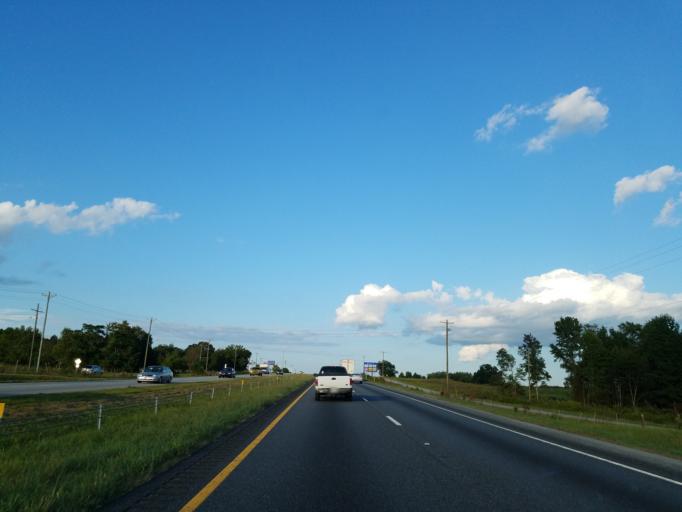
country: US
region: South Carolina
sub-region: Cherokee County
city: Gaffney
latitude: 35.0883
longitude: -81.6956
